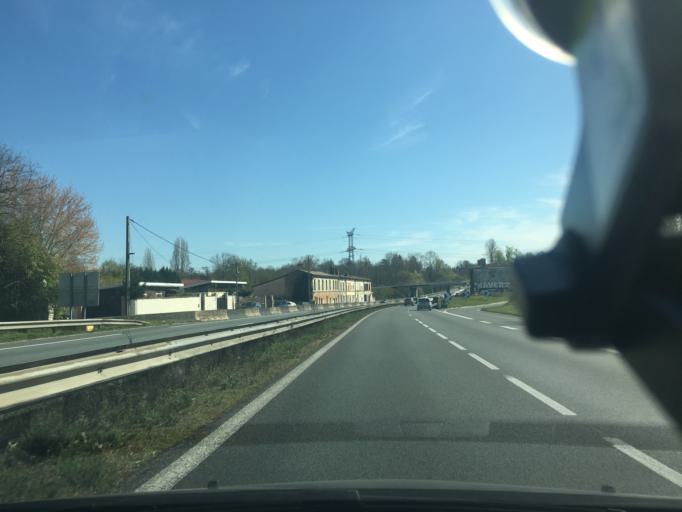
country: FR
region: Aquitaine
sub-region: Departement de la Gironde
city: Montussan
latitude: 44.8779
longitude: -0.4143
